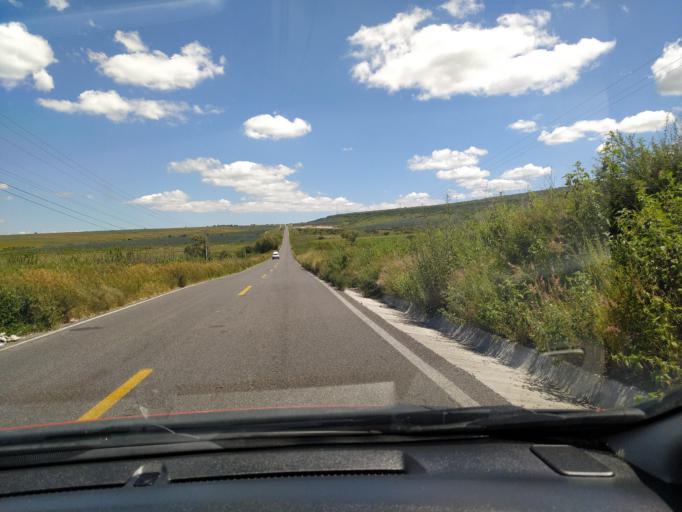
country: MX
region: Jalisco
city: San Diego de Alejandria
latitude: 21.0207
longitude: -101.9475
